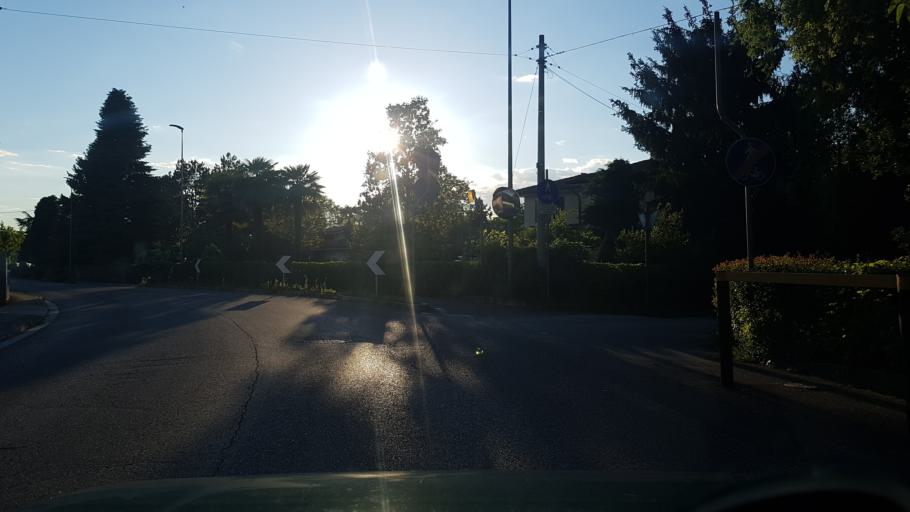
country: IT
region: Friuli Venezia Giulia
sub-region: Provincia di Udine
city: Aiello del Friuli
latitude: 45.8751
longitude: 13.3573
